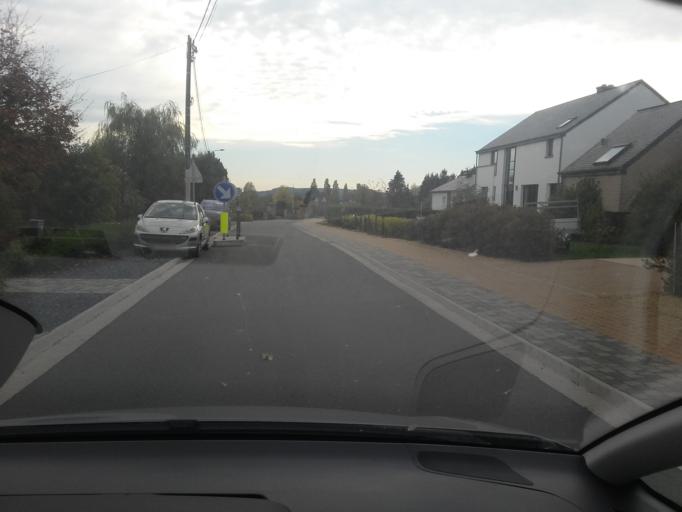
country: BE
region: Wallonia
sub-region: Province du Luxembourg
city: Arlon
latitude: 49.6978
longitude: 5.8179
